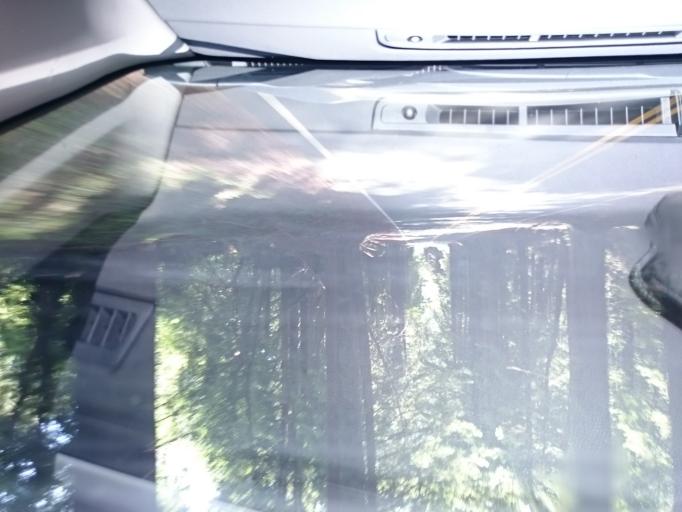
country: US
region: California
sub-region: Mendocino County
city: Fort Bragg
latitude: 39.1687
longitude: -123.6604
